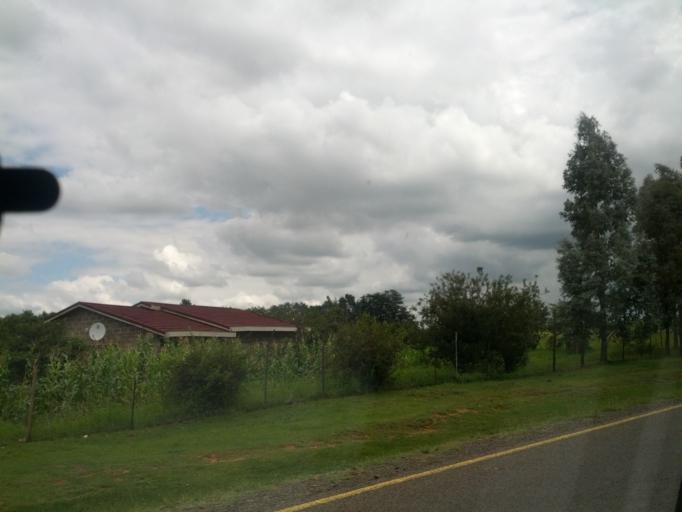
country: LS
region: Leribe
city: Leribe
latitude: -28.9359
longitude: 28.1515
